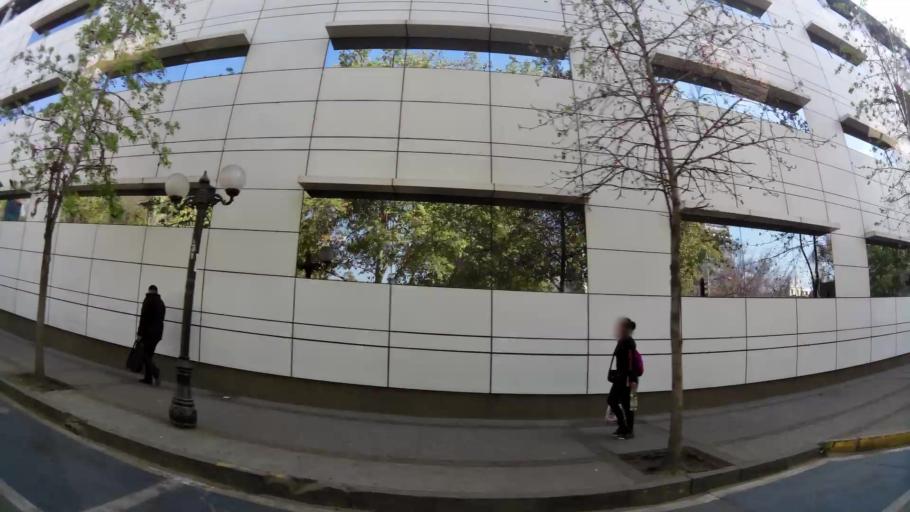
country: CL
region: Santiago Metropolitan
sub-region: Provincia de Santiago
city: Santiago
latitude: -33.4433
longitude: -70.6321
